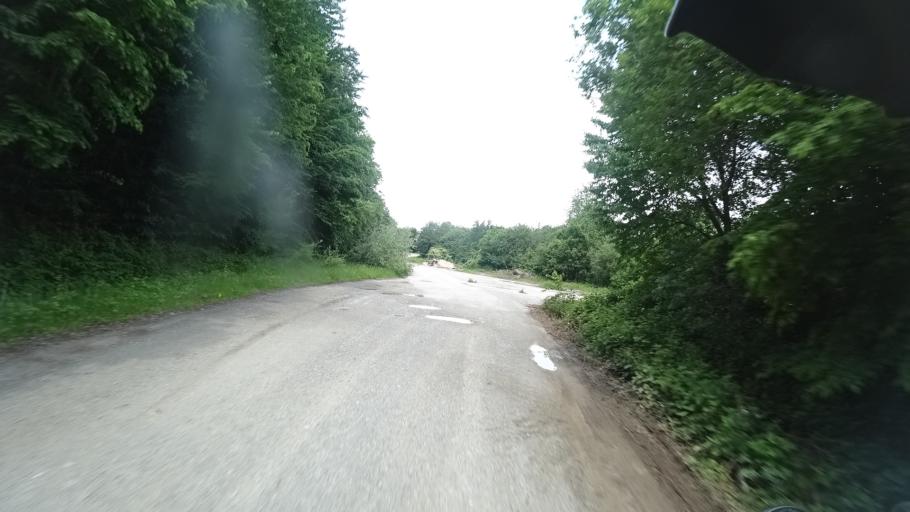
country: HR
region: Sisacko-Moslavacka
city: Gvozd
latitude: 45.3131
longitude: 15.8079
